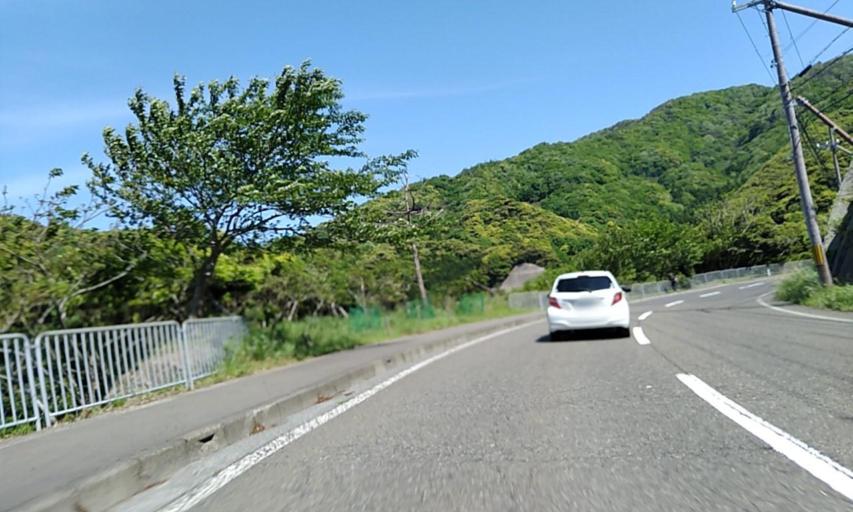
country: JP
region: Fukui
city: Obama
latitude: 35.5257
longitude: 135.7970
